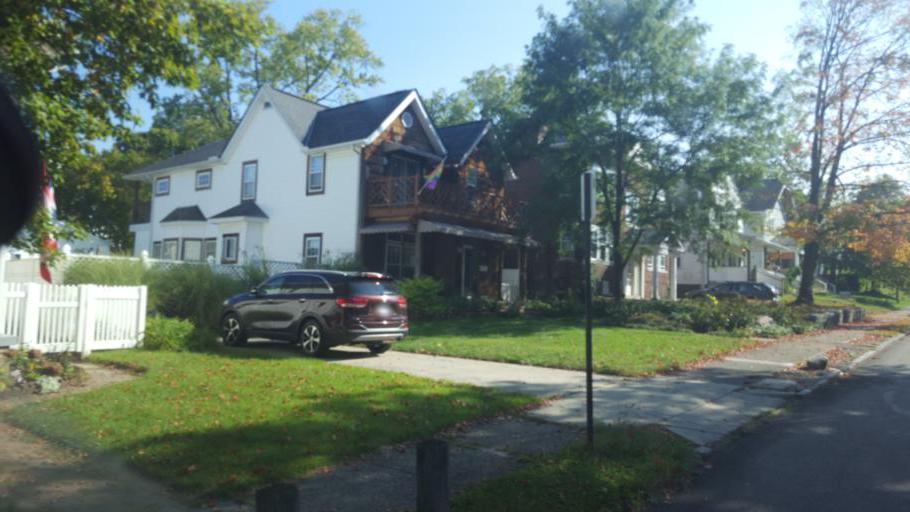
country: US
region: Ohio
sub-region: Franklin County
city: Grandview Heights
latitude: 40.0273
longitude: -83.0123
